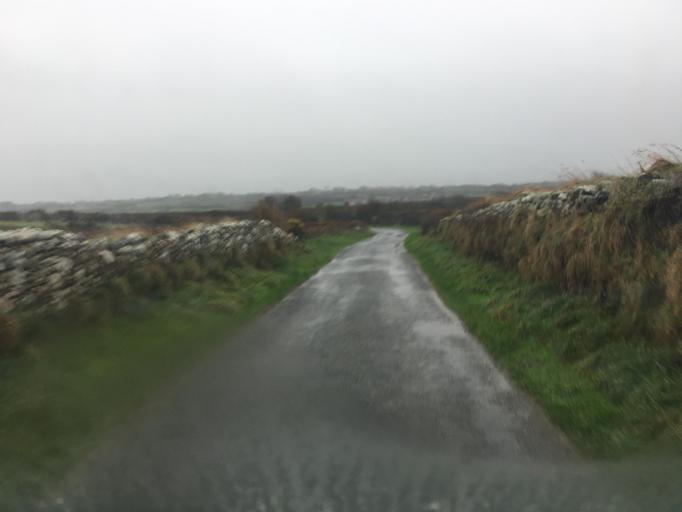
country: FR
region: Lower Normandy
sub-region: Departement de la Manche
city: Beaumont-Hague
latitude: 49.7213
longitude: -1.9217
